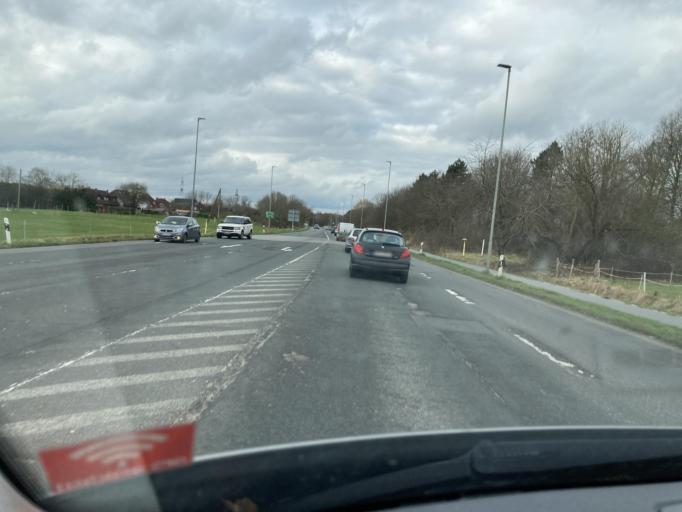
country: DE
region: Lower Saxony
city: Wilhelmshaven
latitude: 53.5503
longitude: 8.0847
